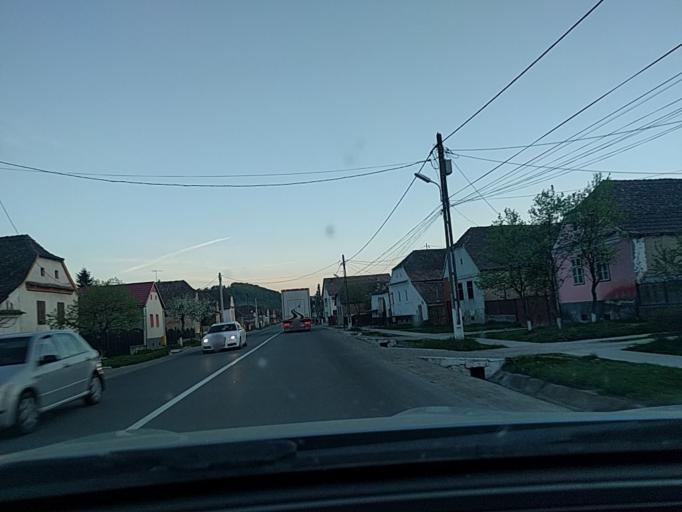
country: RO
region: Mures
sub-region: Comuna Balauseri
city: Chendu
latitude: 46.3544
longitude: 24.7163
